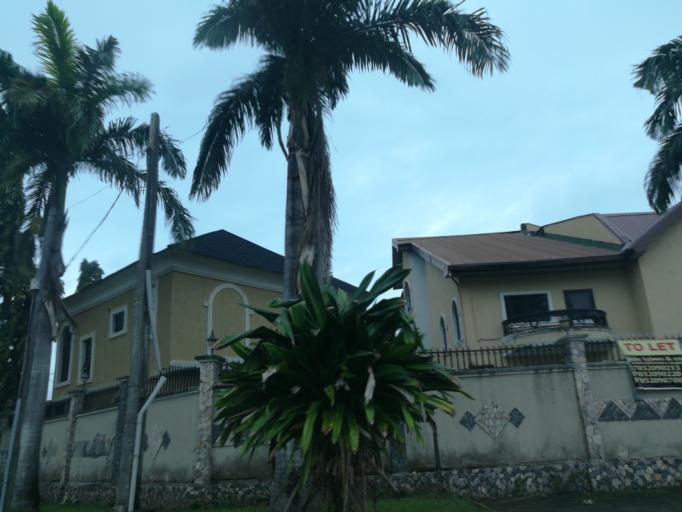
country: NG
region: Lagos
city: Ikoyi
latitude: 6.4397
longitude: 3.4736
